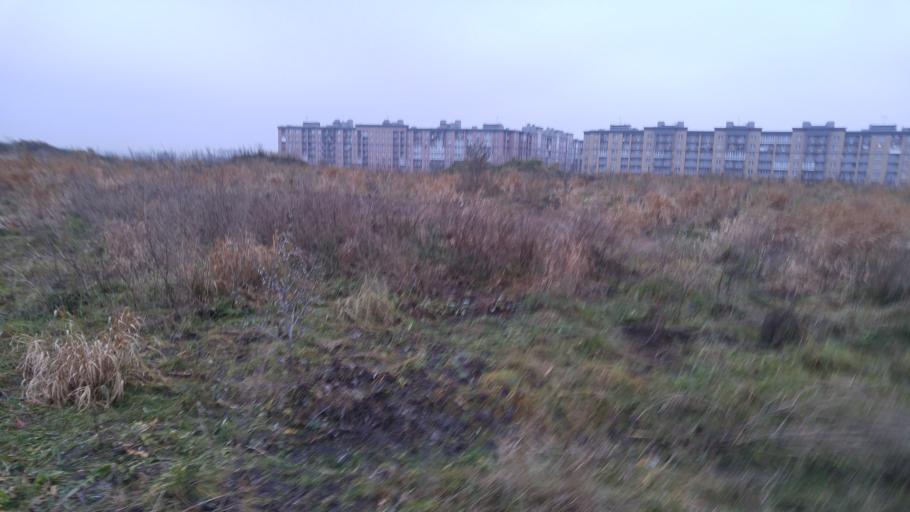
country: RU
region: St.-Petersburg
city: Tyarlevo
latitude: 59.7468
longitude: 30.4869
